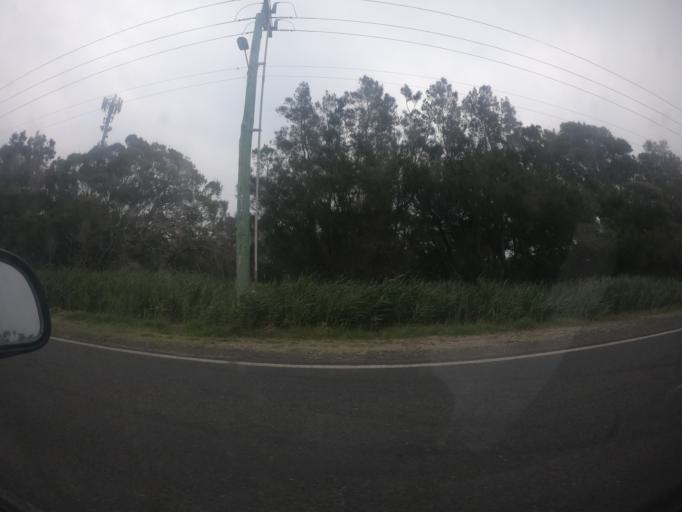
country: AU
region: New South Wales
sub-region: Shellharbour
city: Barrack Heights
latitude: -34.5682
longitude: 150.8665
